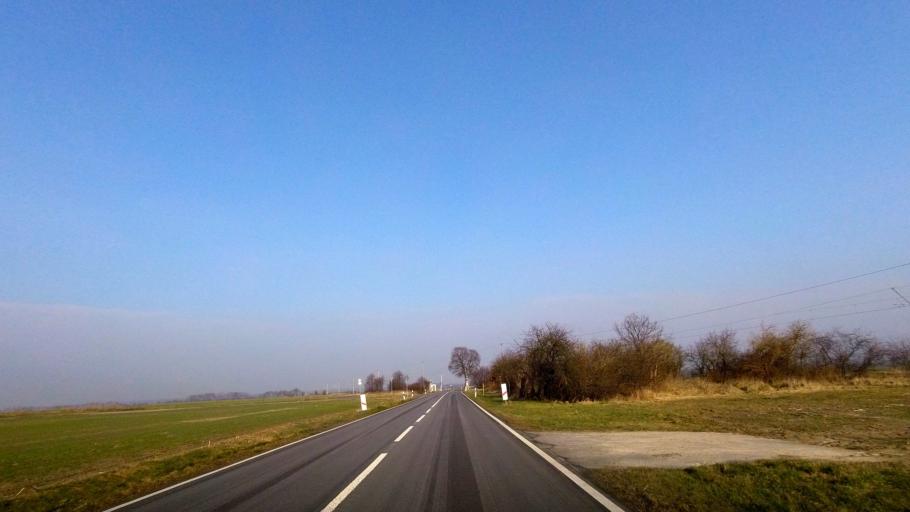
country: DE
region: Brandenburg
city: Juterbog
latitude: 51.9490
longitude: 13.0396
